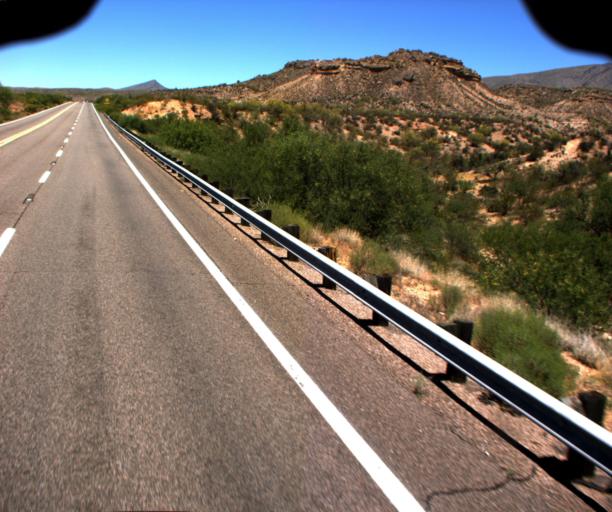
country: US
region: Arizona
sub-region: Pinal County
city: Kearny
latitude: 33.1373
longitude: -110.7882
